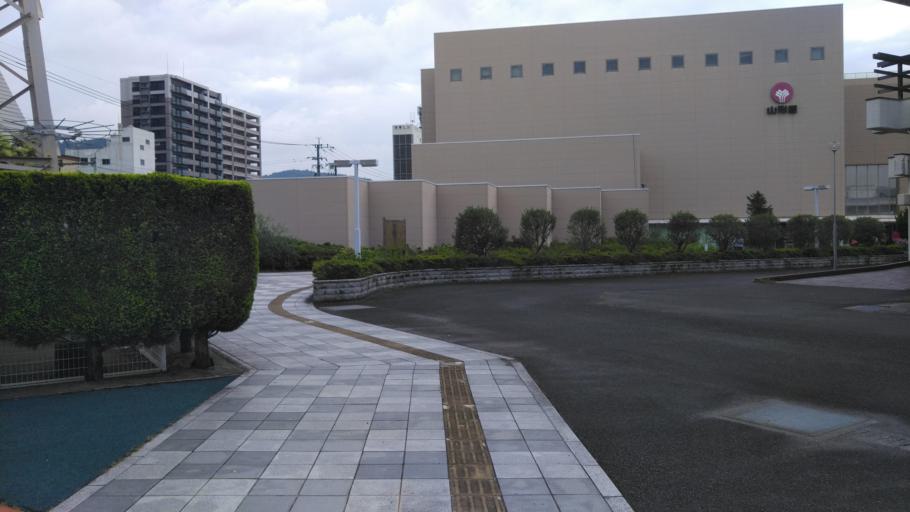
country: JP
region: Kagoshima
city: Kokubu-matsuki
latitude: 31.7404
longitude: 130.7652
